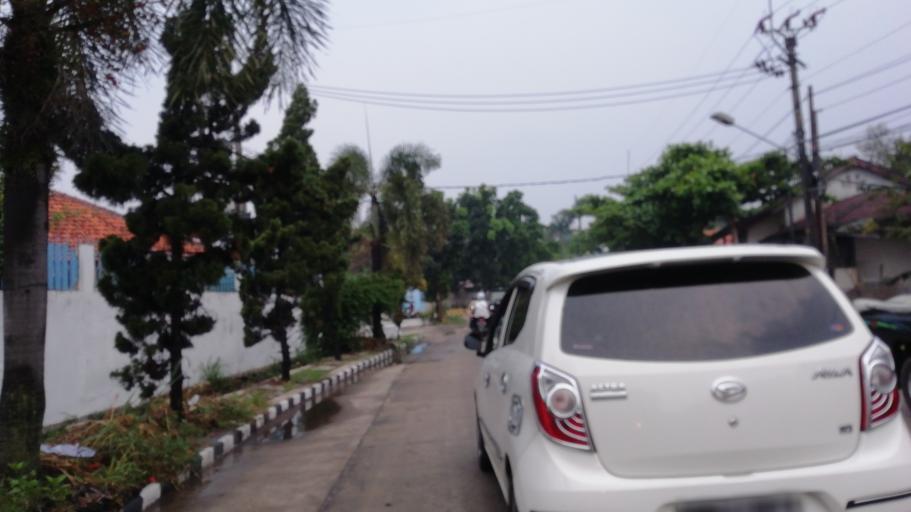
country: ID
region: West Java
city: Bogor
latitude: -6.5564
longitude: 106.8122
